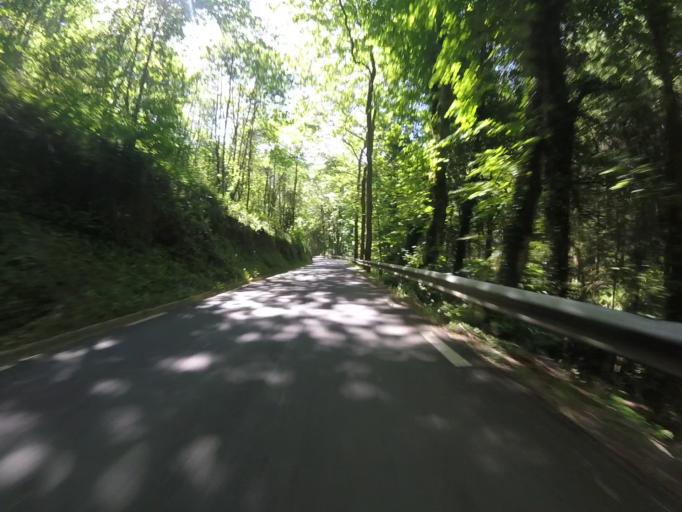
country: ES
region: Basque Country
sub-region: Provincia de Guipuzcoa
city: Albiztur
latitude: 43.1191
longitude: -2.1606
